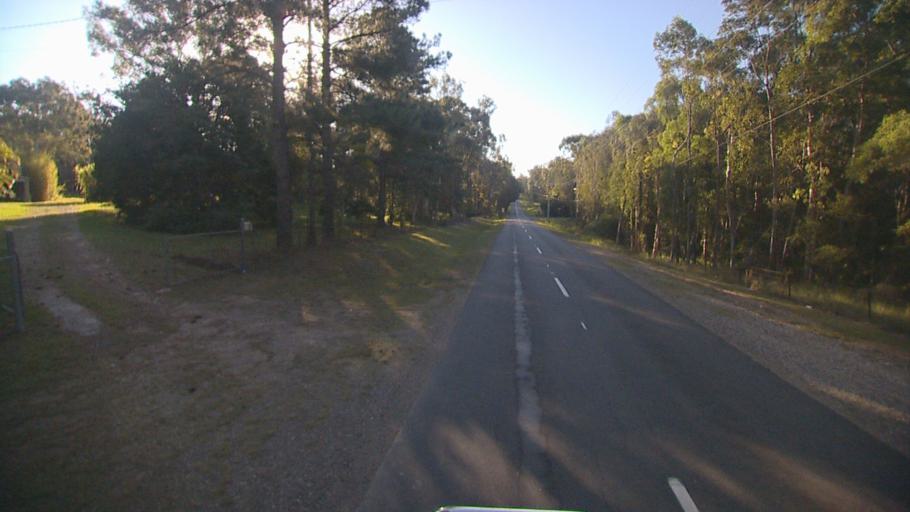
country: AU
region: Queensland
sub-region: Redland
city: Redland Bay
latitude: -27.6724
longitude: 153.2760
